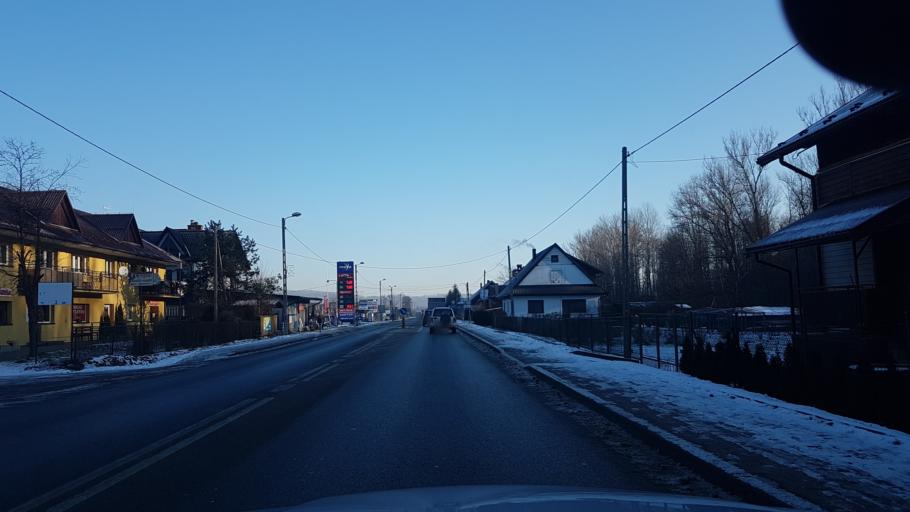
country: PL
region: Lesser Poland Voivodeship
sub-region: Powiat nowosadecki
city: Olszana
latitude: 49.5299
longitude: 20.5181
